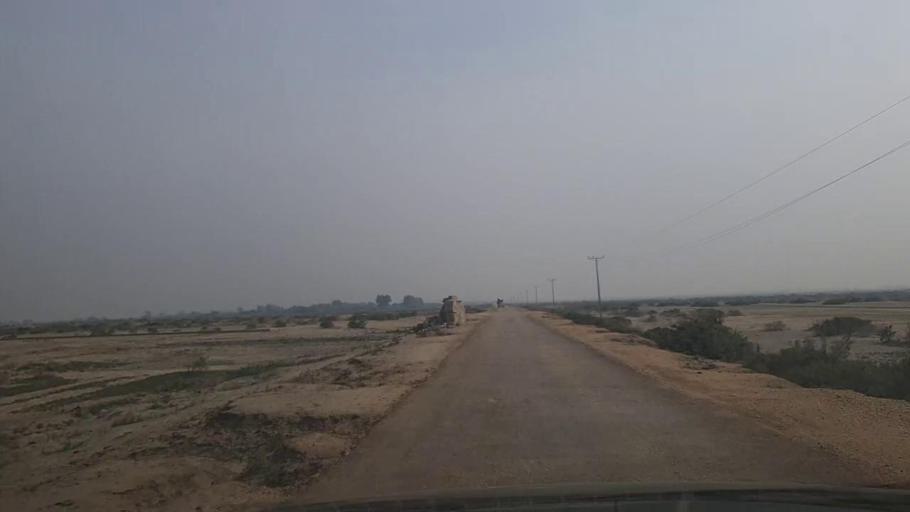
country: PK
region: Sindh
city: Mirpur Sakro
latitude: 24.4629
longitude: 67.6899
